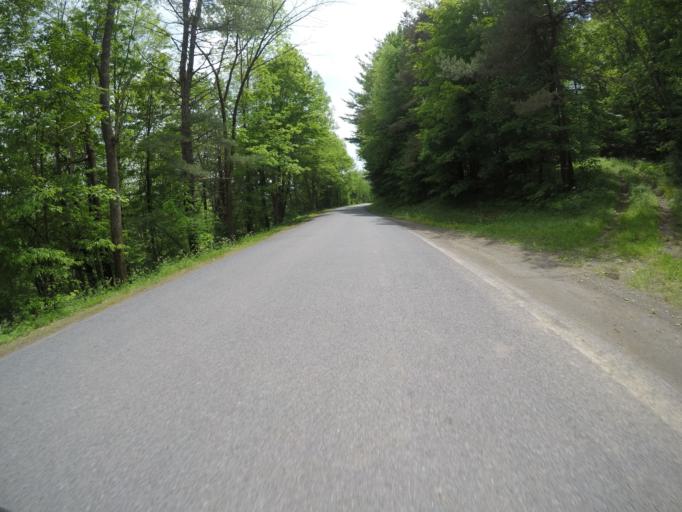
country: US
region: New York
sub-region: Delaware County
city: Stamford
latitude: 42.2348
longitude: -74.6960
